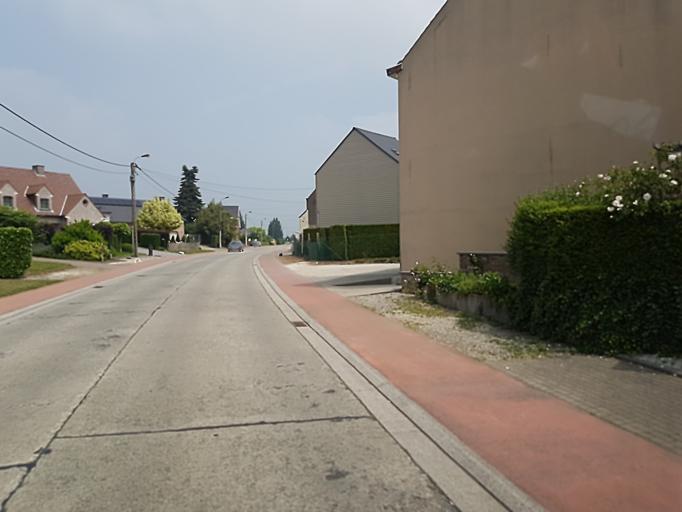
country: BE
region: Flanders
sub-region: Provincie Oost-Vlaanderen
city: Geraardsbergen
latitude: 50.8011
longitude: 3.8984
